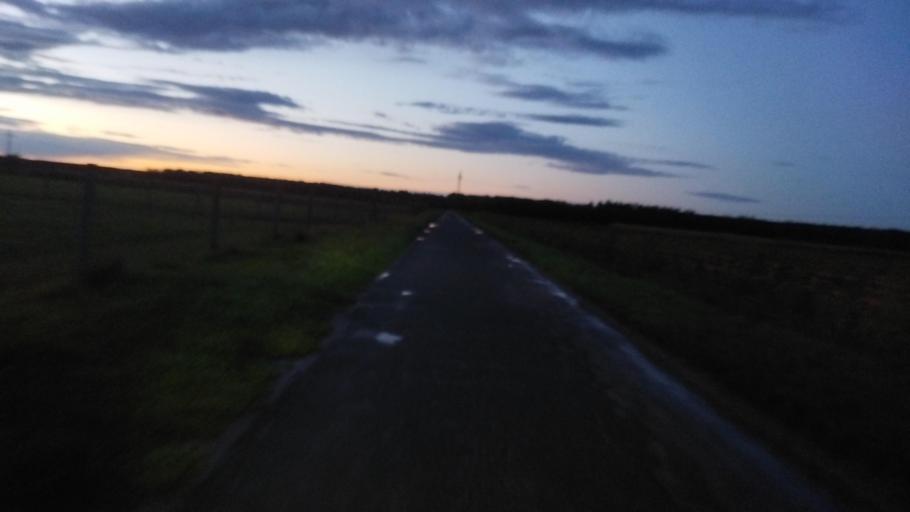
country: DE
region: Hesse
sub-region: Regierungsbezirk Darmstadt
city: Einhausen
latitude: 49.6787
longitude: 8.5153
